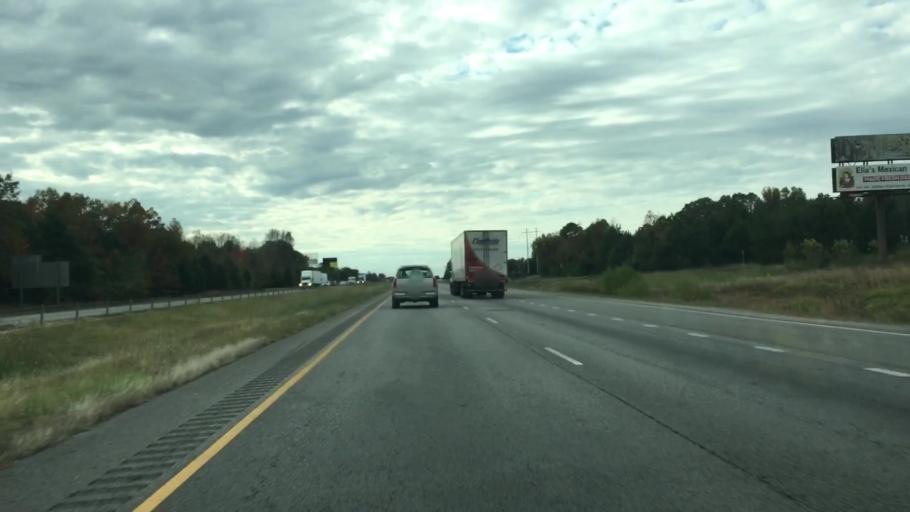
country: US
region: Arkansas
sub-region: Conway County
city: Morrilton
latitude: 35.1629
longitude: -92.6459
